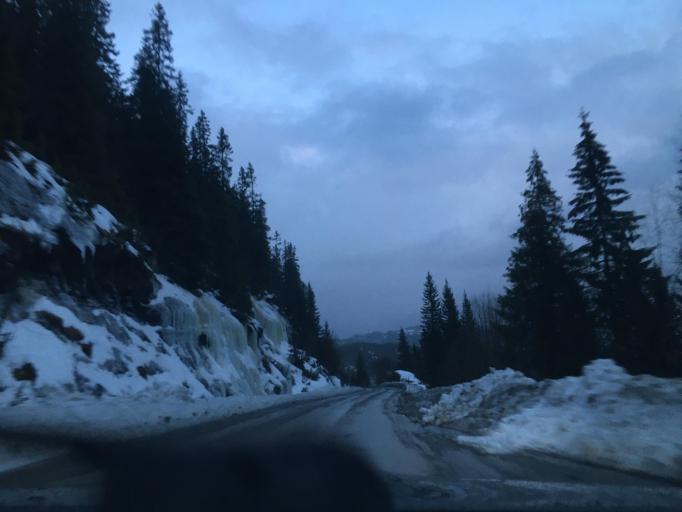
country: NO
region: Nordland
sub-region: Rana
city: Hauknes
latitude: 66.2974
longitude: 13.9224
